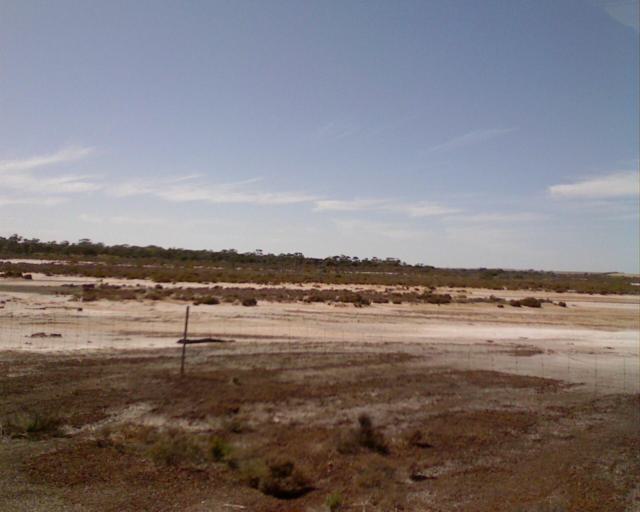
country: AU
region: Western Australia
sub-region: Moora
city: Moora
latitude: -30.1075
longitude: 116.2584
